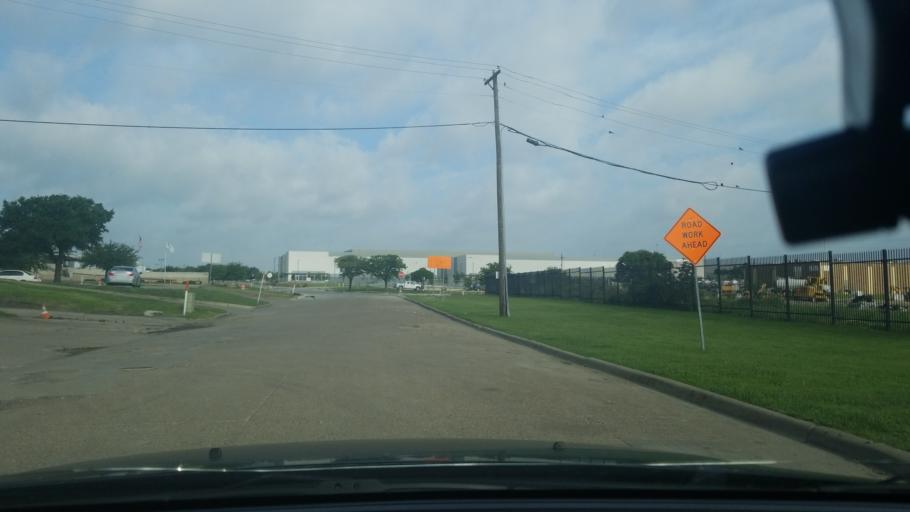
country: US
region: Texas
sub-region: Dallas County
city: Mesquite
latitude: 32.7748
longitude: -96.6455
